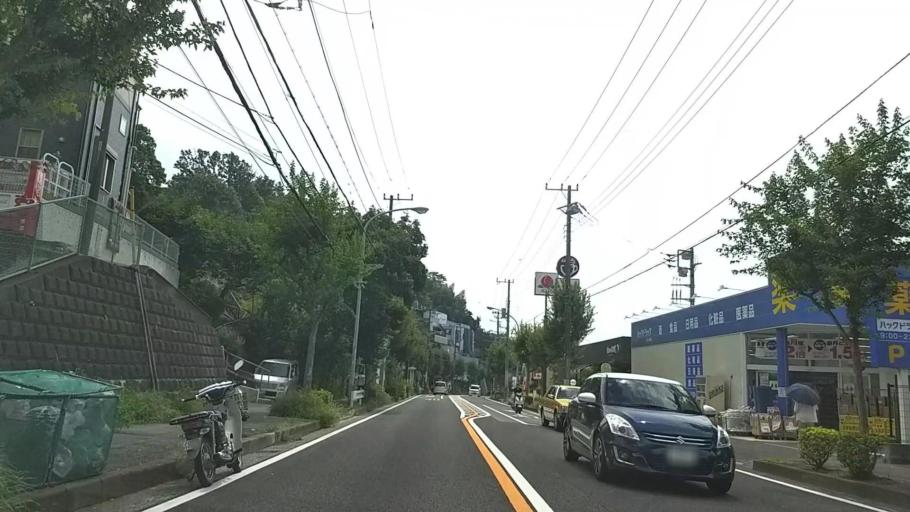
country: JP
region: Kanagawa
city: Yokohama
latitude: 35.4264
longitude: 139.5825
